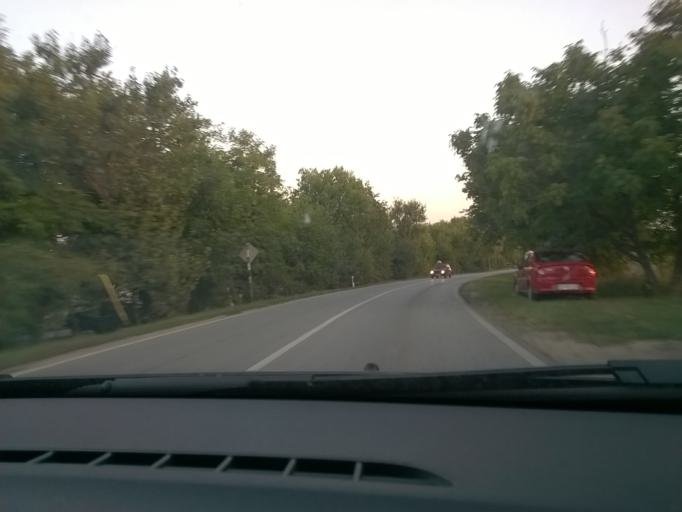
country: RS
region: Autonomna Pokrajina Vojvodina
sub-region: Juznobanatski Okrug
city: Vrsac
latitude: 45.1057
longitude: 21.2982
